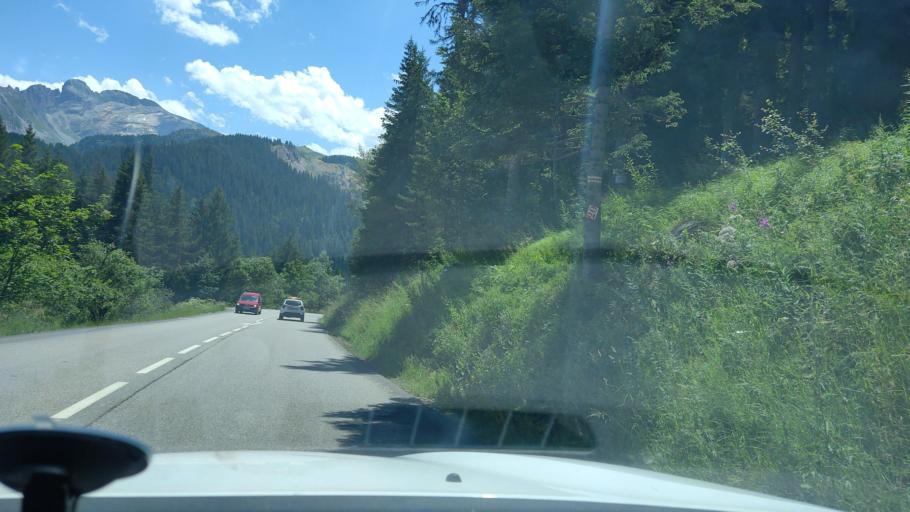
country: FR
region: Rhone-Alpes
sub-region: Departement de la Savoie
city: Courchevel
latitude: 45.4125
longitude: 6.6407
